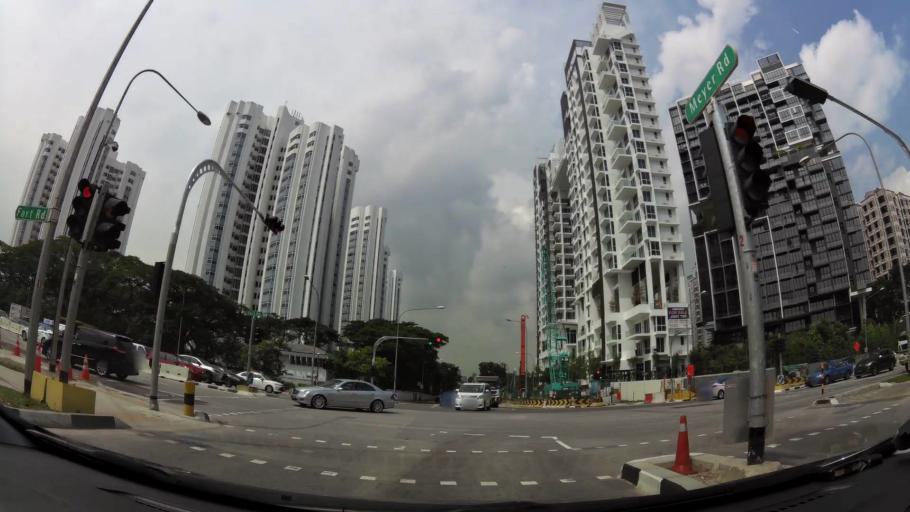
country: SG
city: Singapore
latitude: 1.2979
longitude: 103.8857
